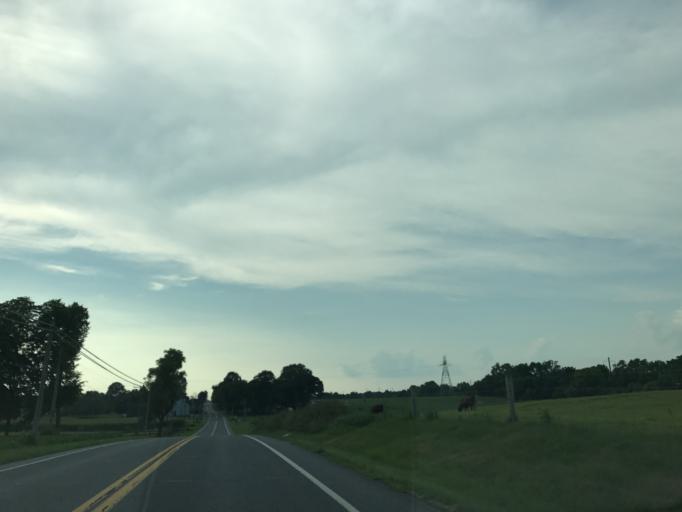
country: US
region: Pennsylvania
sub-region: Lancaster County
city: Rheems
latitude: 40.1201
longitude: -76.5420
